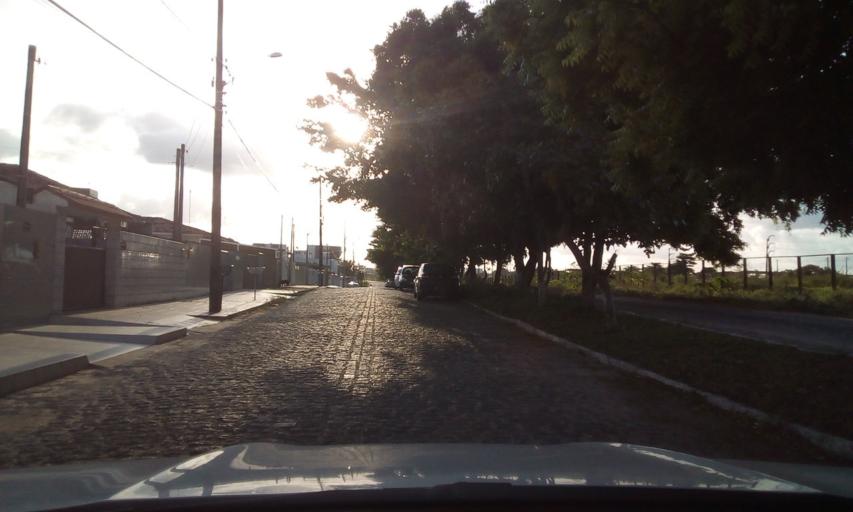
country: BR
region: Paraiba
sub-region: Joao Pessoa
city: Joao Pessoa
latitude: -7.1862
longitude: -34.8744
